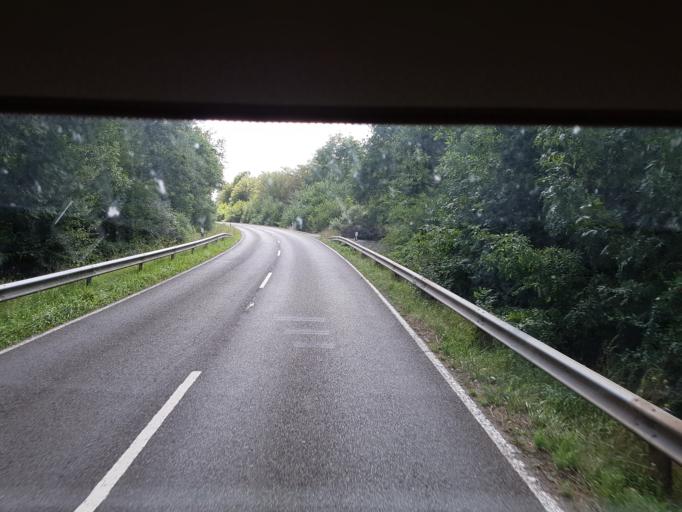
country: DE
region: Rheinland-Pfalz
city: Bekond
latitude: 49.8688
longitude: 6.7899
